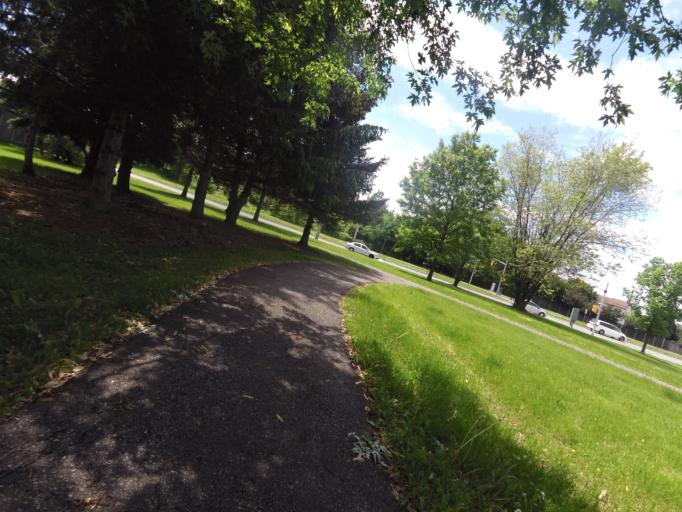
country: CA
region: Ontario
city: Ottawa
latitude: 45.3669
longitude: -75.6199
